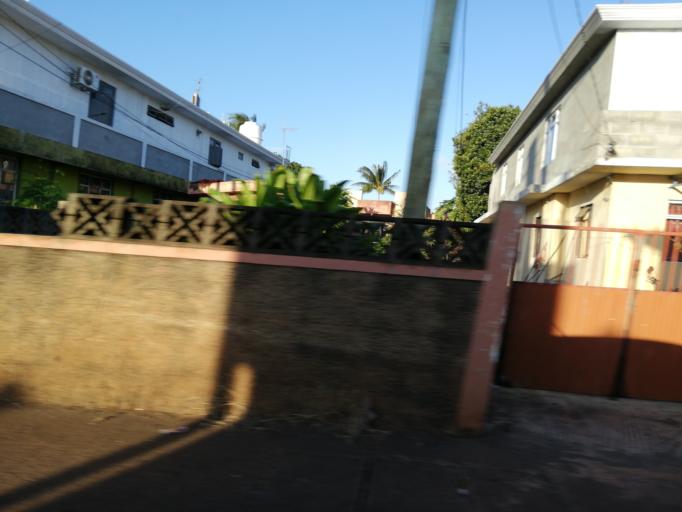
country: MU
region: Pamplemousses
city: Terre Rouge
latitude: -20.1233
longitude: 57.5316
